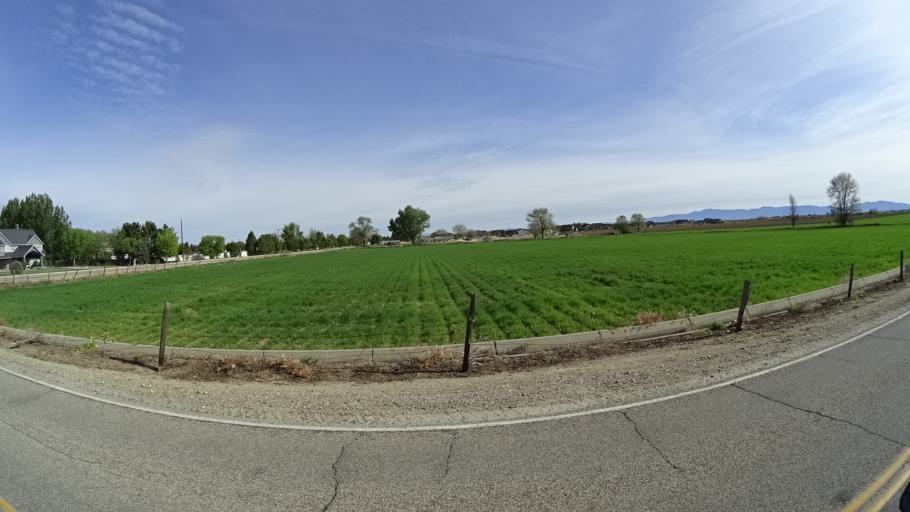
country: US
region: Idaho
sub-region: Ada County
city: Kuna
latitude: 43.4736
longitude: -116.4030
